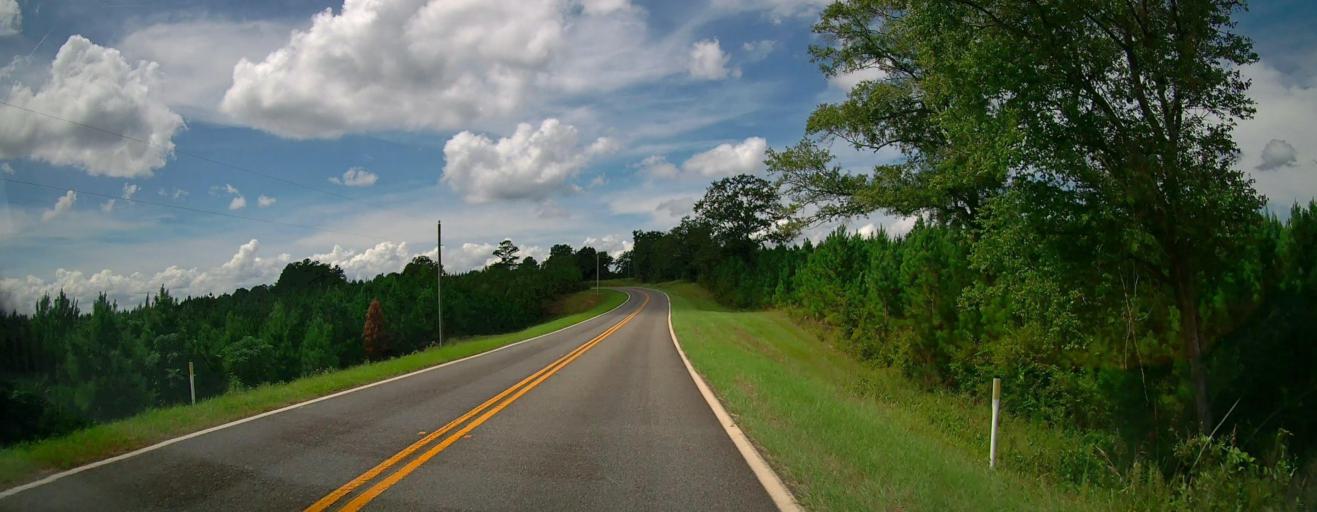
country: US
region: Georgia
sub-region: Taylor County
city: Butler
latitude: 32.4350
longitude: -84.1884
